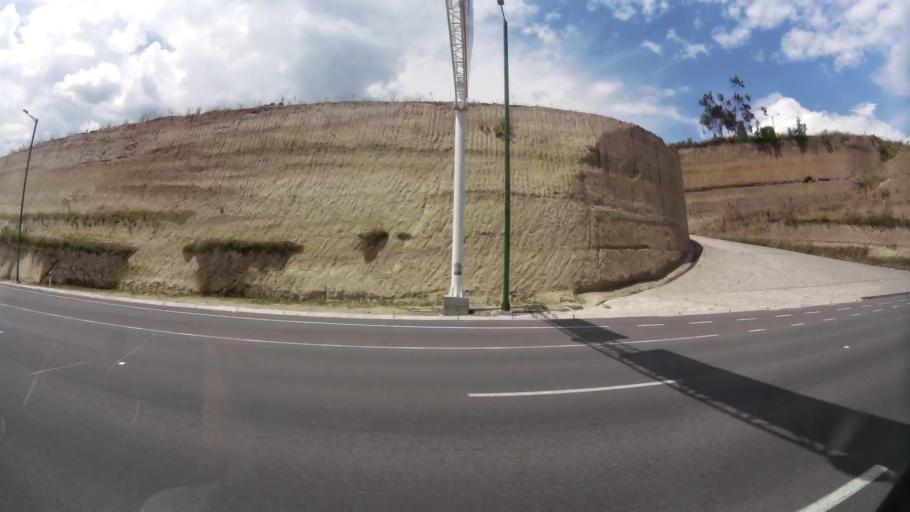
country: EC
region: Pichincha
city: Sangolqui
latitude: -0.2160
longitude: -78.3355
